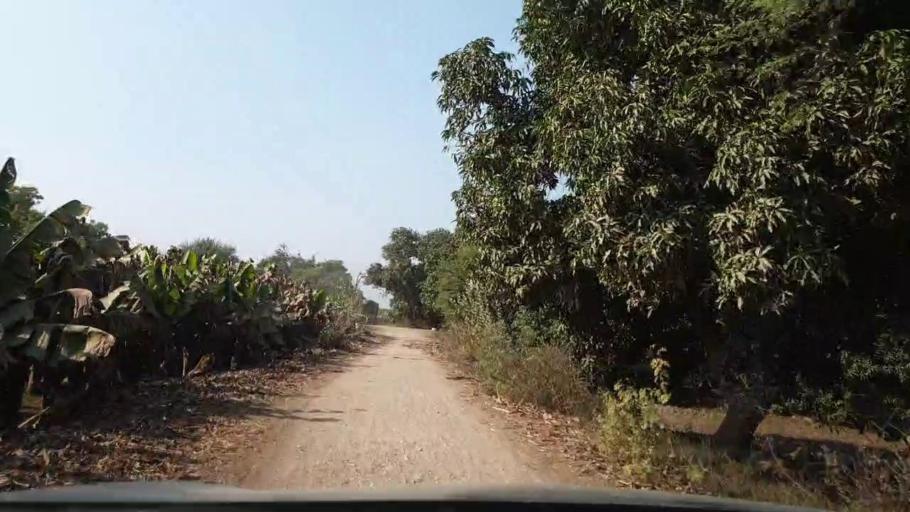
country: PK
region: Sindh
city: Tando Allahyar
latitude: 25.5478
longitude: 68.7695
